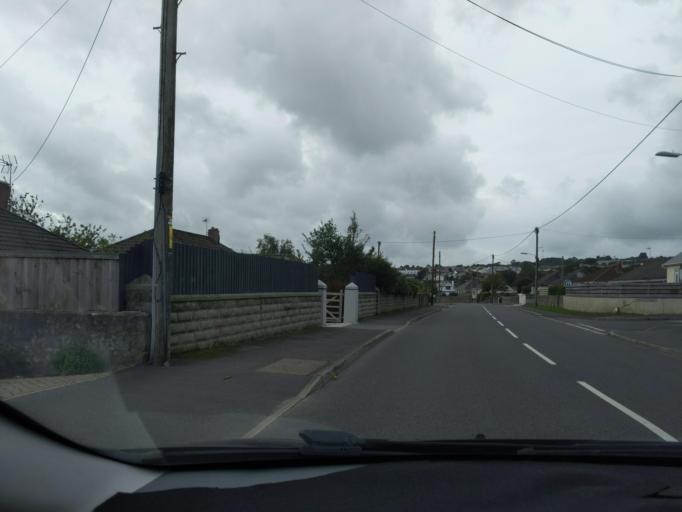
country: GB
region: England
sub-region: Cornwall
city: St Austell
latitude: 50.3437
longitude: -4.7658
